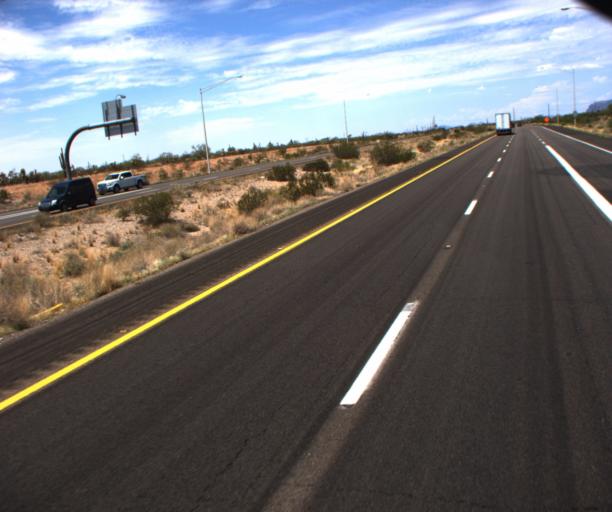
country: US
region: Arizona
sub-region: Pinal County
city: Gold Camp
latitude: 33.2606
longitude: -111.3439
